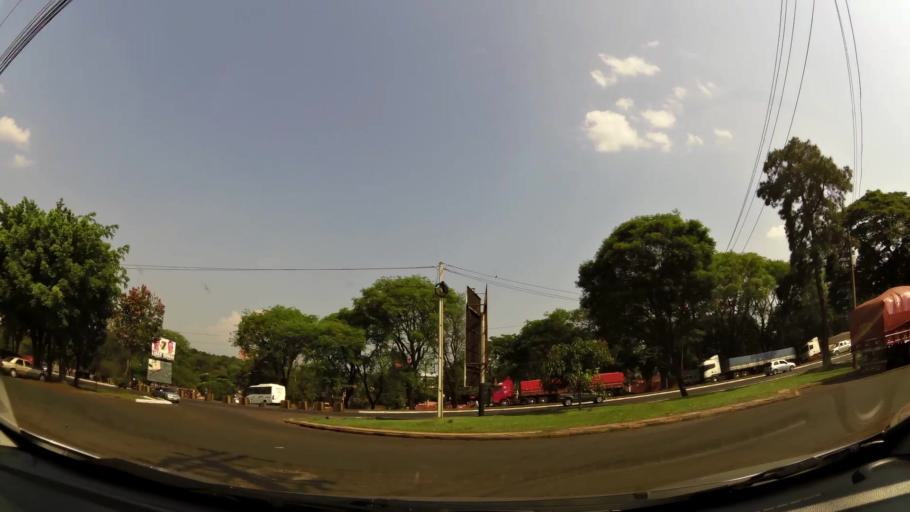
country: PY
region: Alto Parana
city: Ciudad del Este
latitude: -25.5095
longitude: -54.6204
